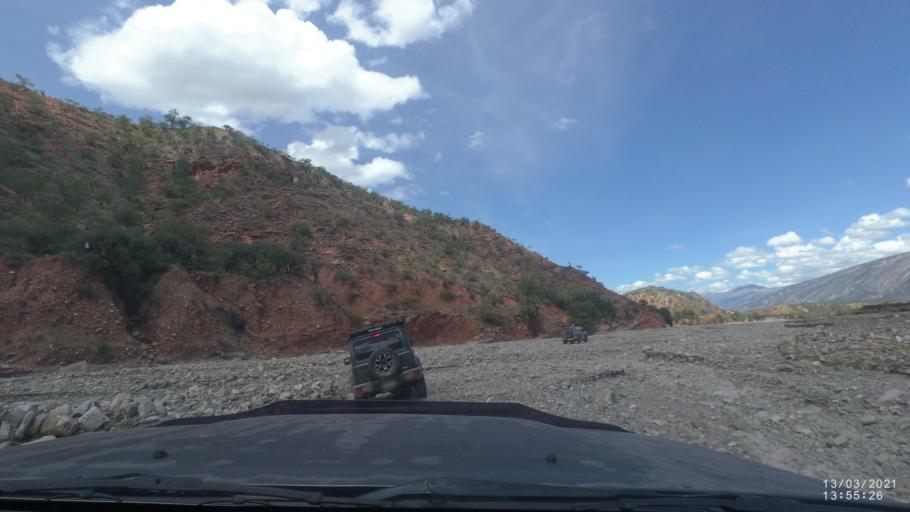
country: BO
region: Cochabamba
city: Cliza
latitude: -17.9343
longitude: -65.8656
